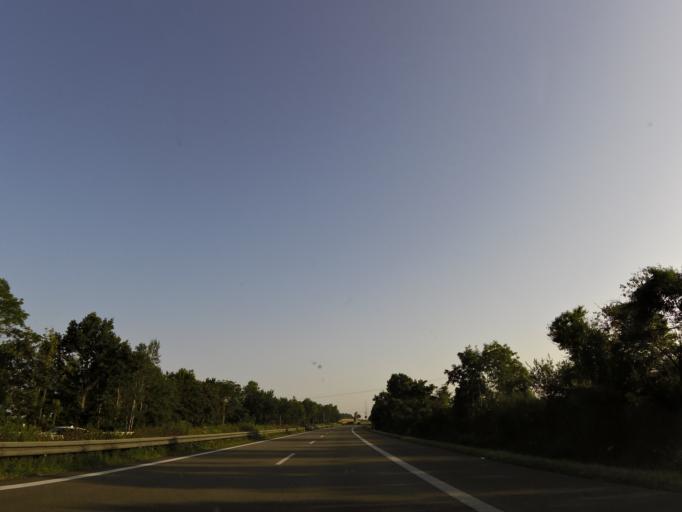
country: DE
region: Bavaria
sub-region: Swabia
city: Bellenberg
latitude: 48.2476
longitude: 10.1157
